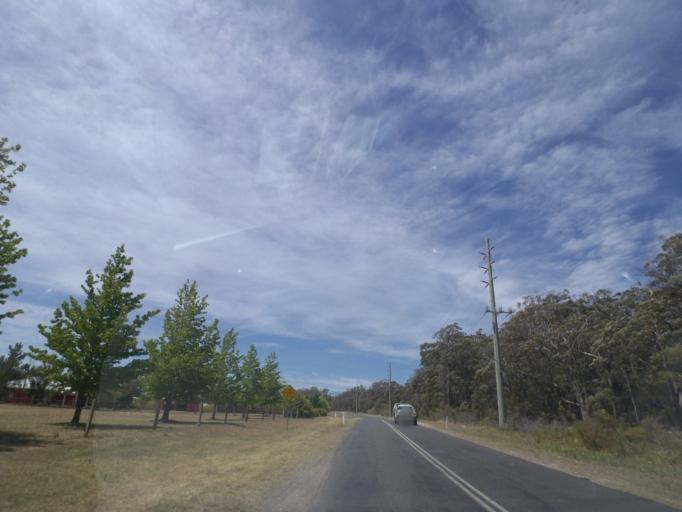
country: AU
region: New South Wales
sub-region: Wingecarribee
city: Colo Vale
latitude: -34.3803
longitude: 150.5336
